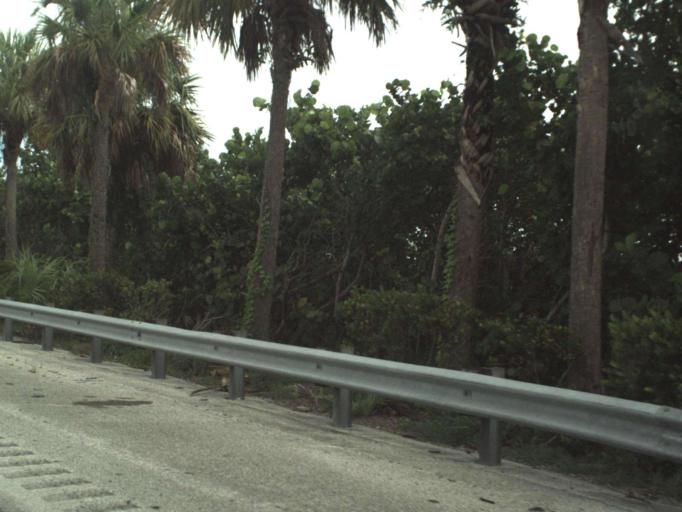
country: US
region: Florida
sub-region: Martin County
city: Palm City
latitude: 27.1190
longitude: -80.2685
